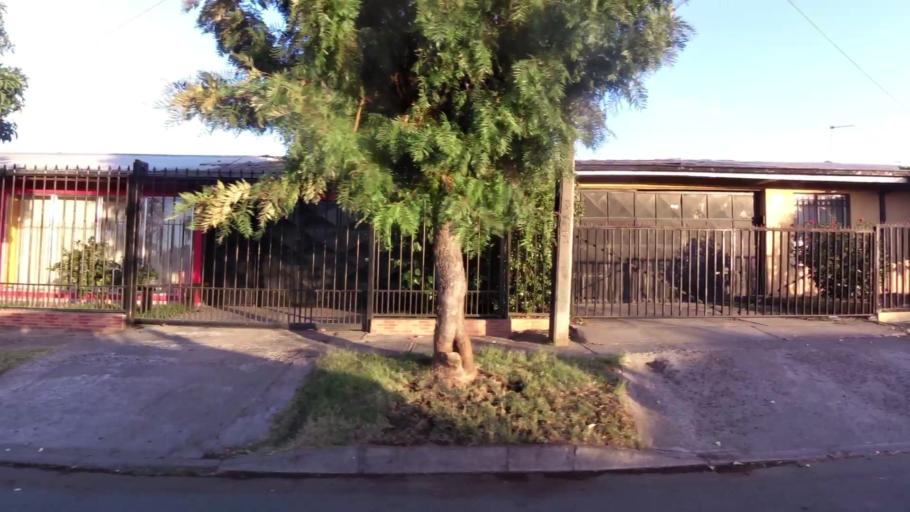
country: CL
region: Maule
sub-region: Provincia de Talca
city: Talca
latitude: -35.4439
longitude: -71.6365
